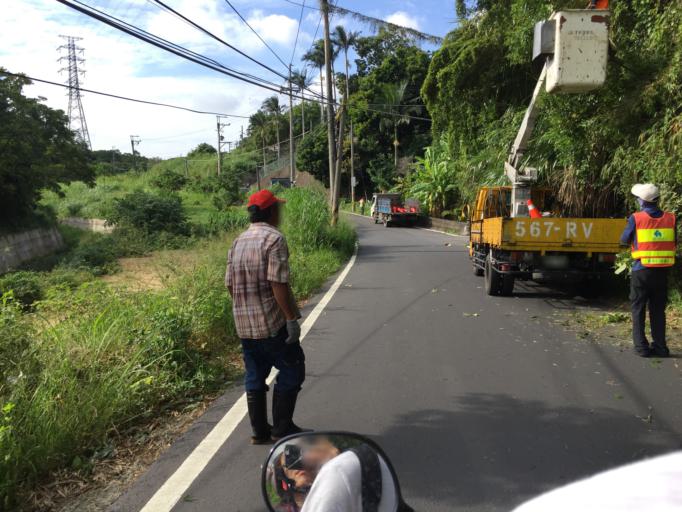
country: TW
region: Taiwan
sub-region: Hsinchu
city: Hsinchu
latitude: 24.7654
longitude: 120.9412
